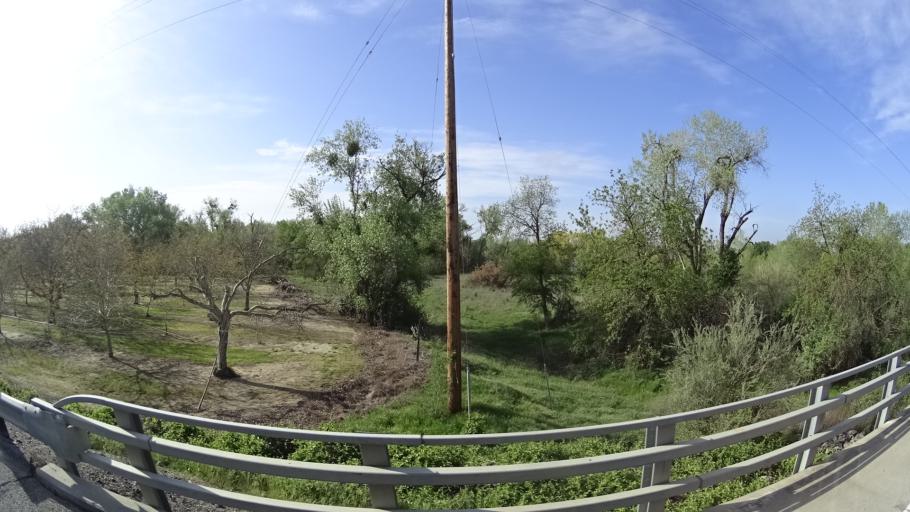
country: US
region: California
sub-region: Glenn County
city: Hamilton City
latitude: 39.6292
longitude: -121.9905
